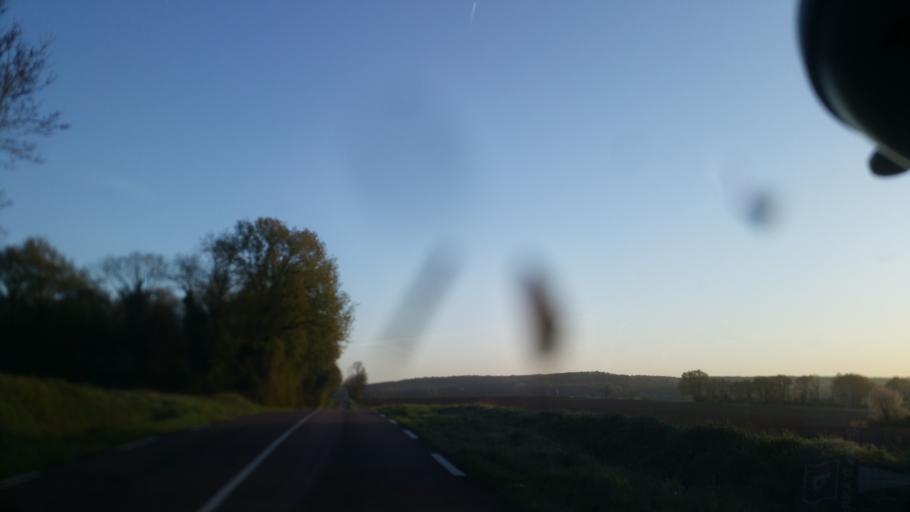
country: FR
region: Ile-de-France
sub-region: Departement de l'Essonne
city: Saint-Cyr-sous-Dourdan
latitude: 48.5608
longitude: 2.0282
